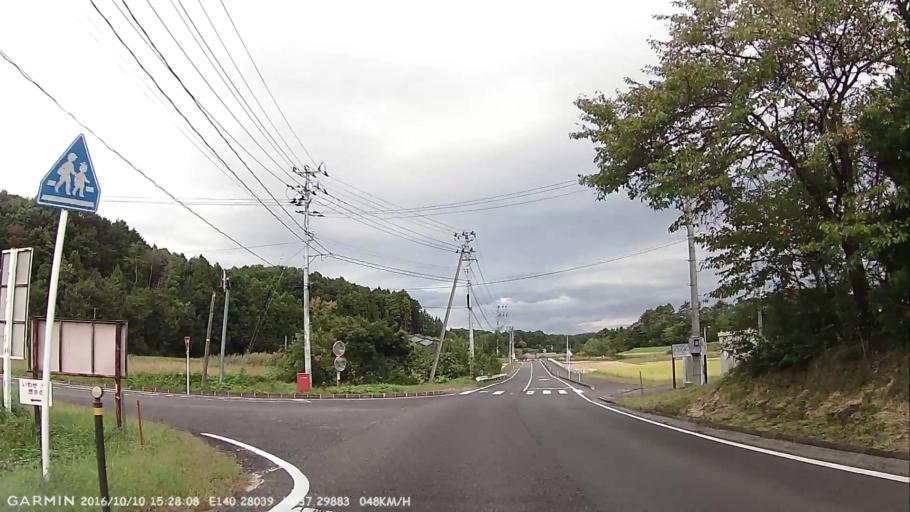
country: JP
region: Fukushima
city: Sukagawa
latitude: 37.2989
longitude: 140.2802
